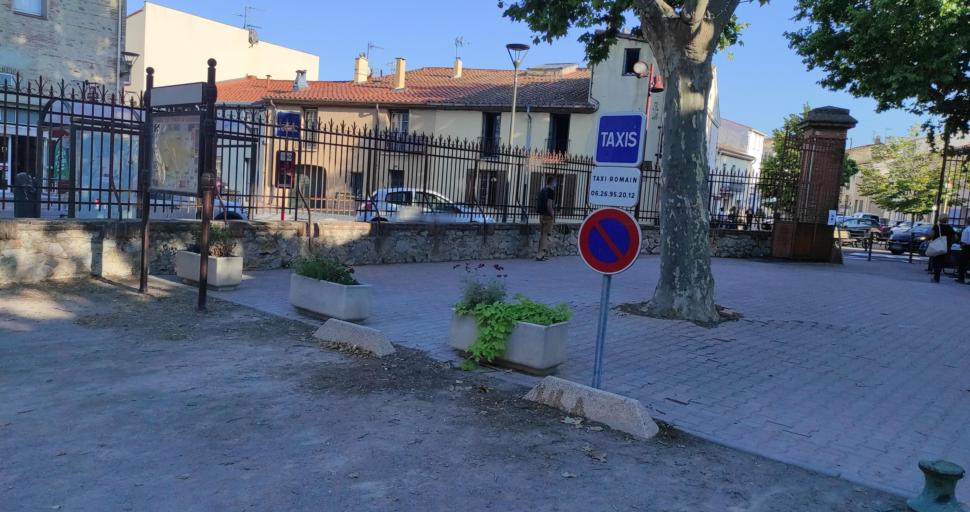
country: FR
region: Languedoc-Roussillon
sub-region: Departement des Pyrenees-Orientales
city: Alenya
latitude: 42.6393
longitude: 2.9807
